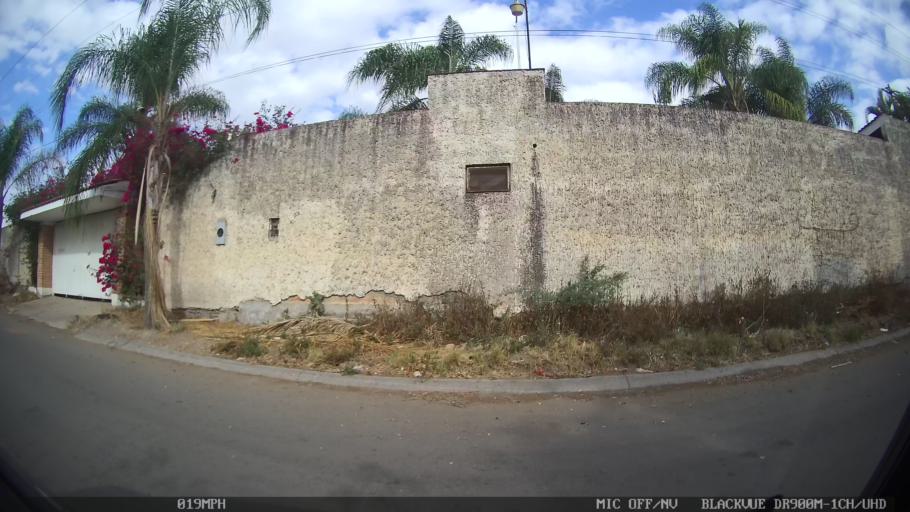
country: MX
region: Jalisco
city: Tonala
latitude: 20.6582
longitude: -103.2343
